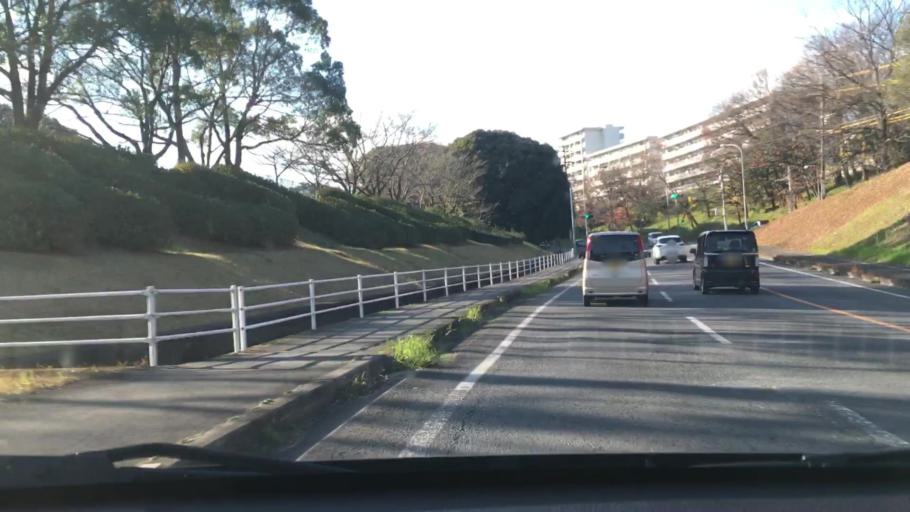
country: JP
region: Oita
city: Oita
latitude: 33.2251
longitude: 131.6515
